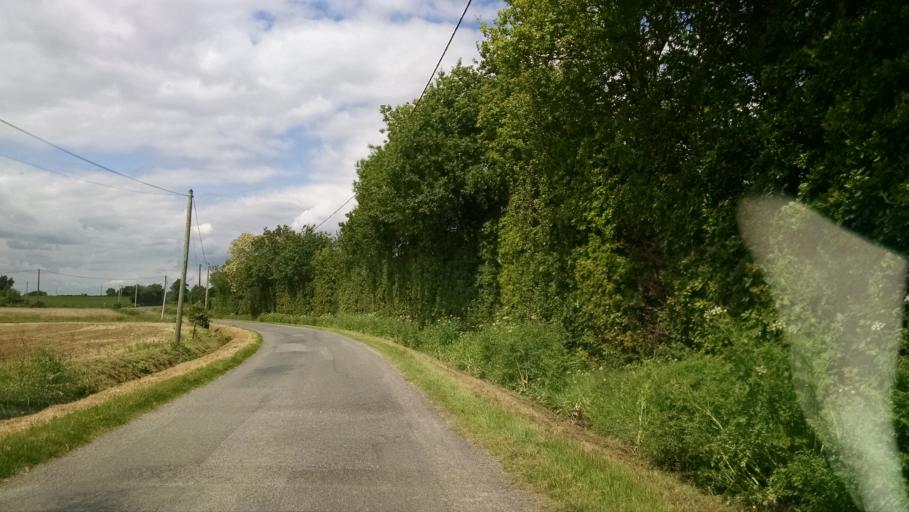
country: FR
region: Pays de la Loire
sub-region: Departement de la Vendee
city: Saint-Hilaire-de-Loulay
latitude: 47.0083
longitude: -1.3730
